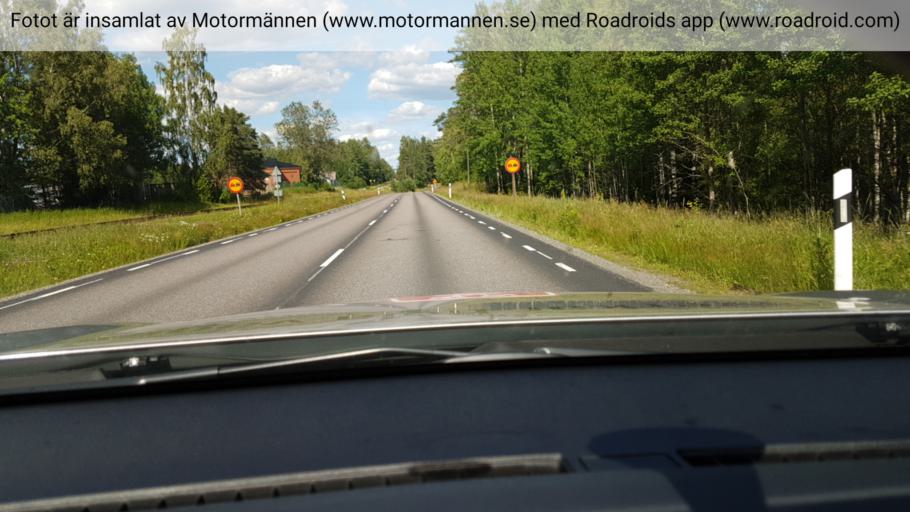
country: SE
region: Joenkoeping
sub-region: Vaggeryds Kommun
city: Vaggeryd
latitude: 57.4839
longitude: 14.1163
